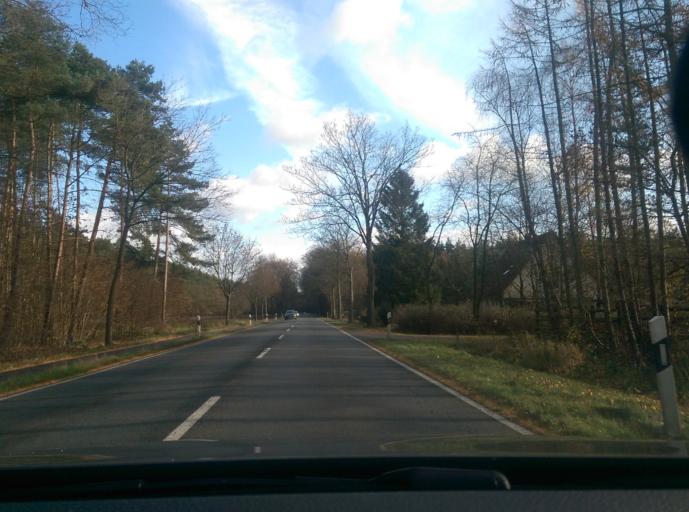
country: DE
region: Lower Saxony
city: Winsen
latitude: 52.6750
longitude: 9.9386
